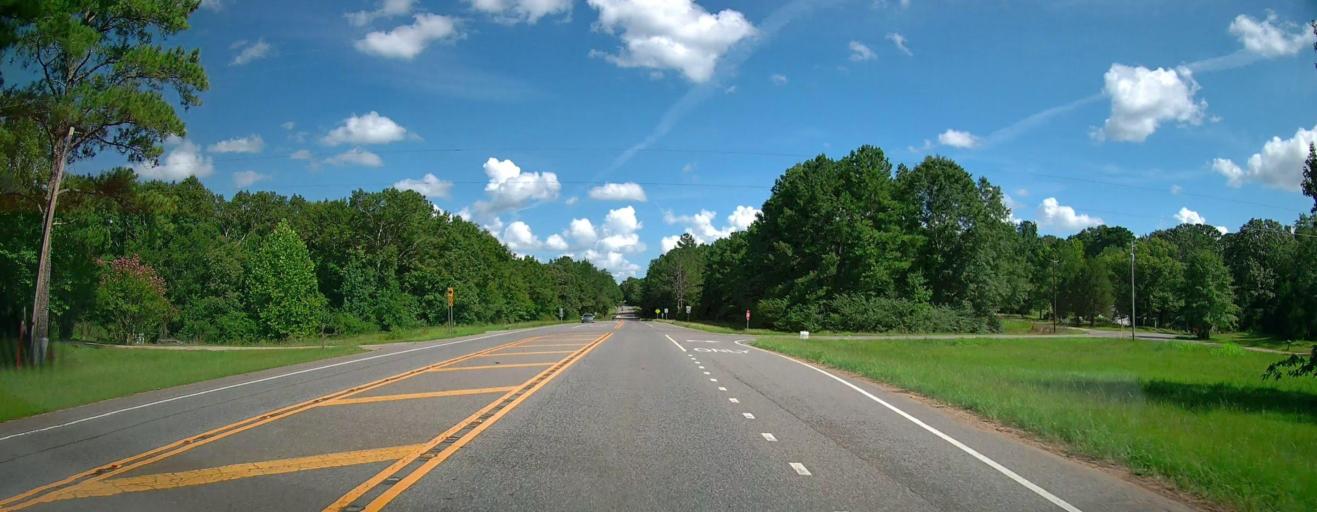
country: US
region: Alabama
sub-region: Pickens County
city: Gordo
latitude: 33.2968
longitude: -87.8770
